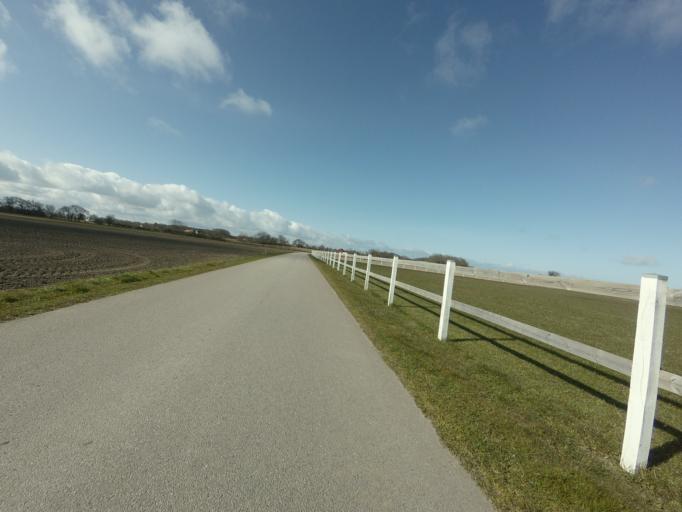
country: SE
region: Skane
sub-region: Hoganas Kommun
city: Hoganas
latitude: 56.1842
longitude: 12.6105
